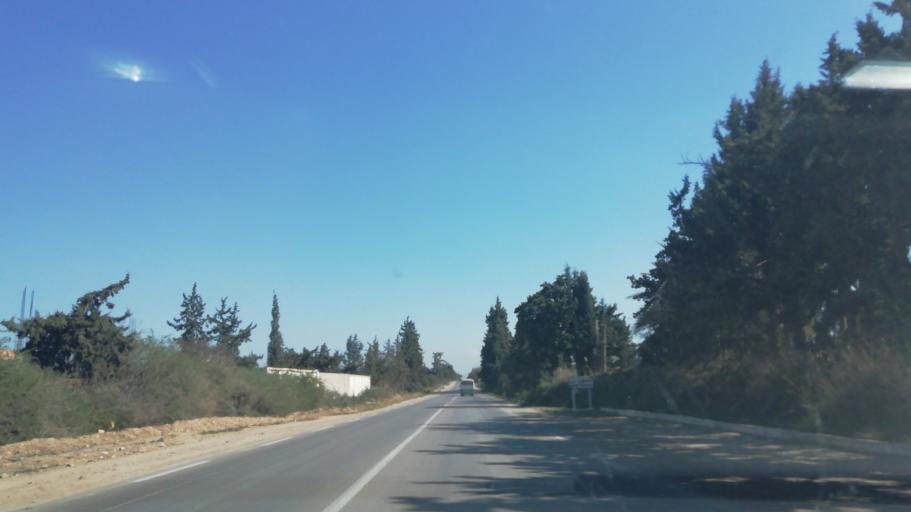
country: DZ
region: Mascara
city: Sig
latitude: 35.5653
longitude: -0.0840
